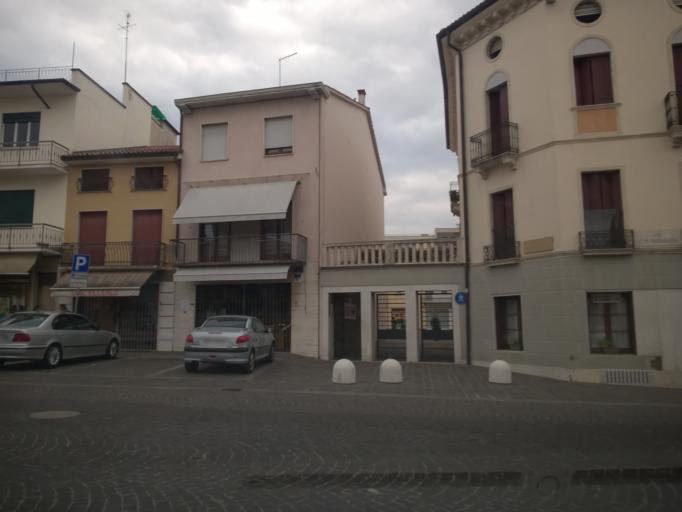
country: IT
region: Veneto
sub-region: Provincia di Vicenza
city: Thiene
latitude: 45.7093
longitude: 11.4744
